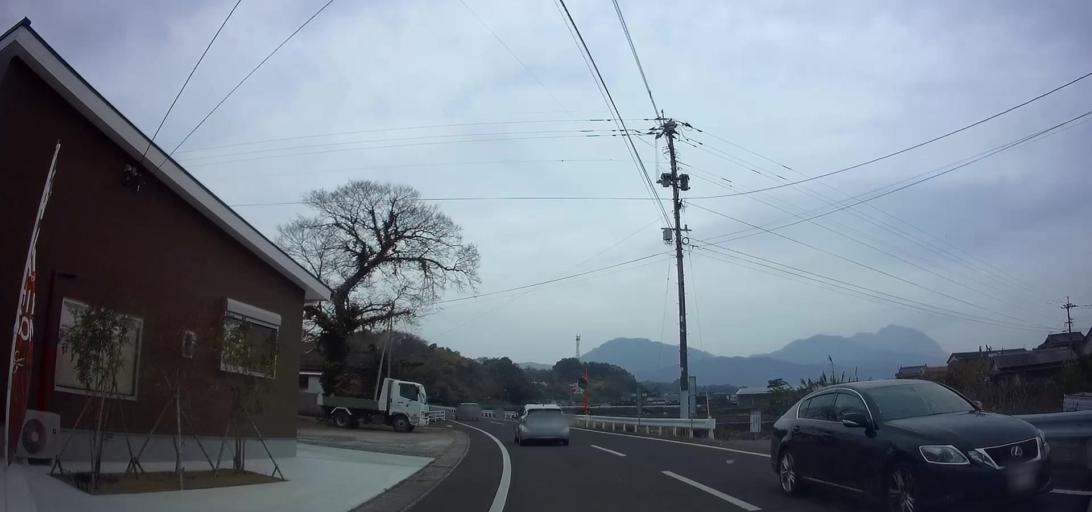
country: JP
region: Nagasaki
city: Shimabara
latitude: 32.6651
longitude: 130.3000
